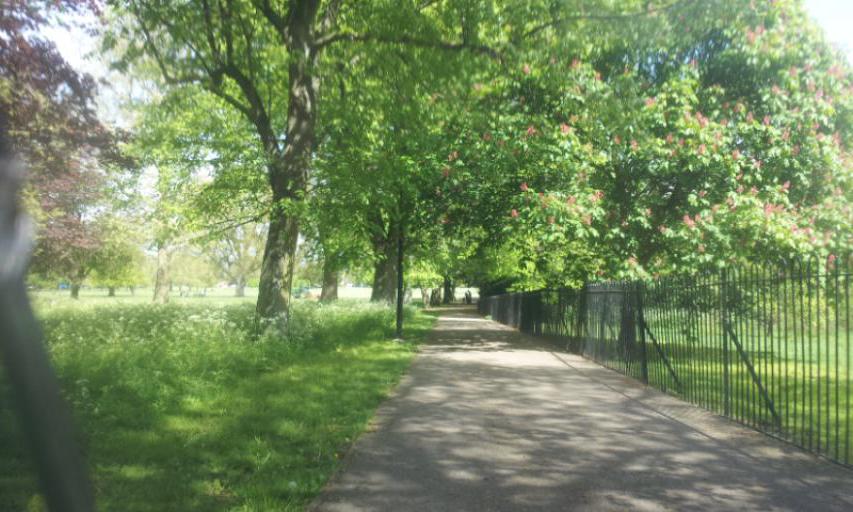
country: GB
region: England
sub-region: Greater London
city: Camberwell
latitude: 51.4569
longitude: -0.0644
